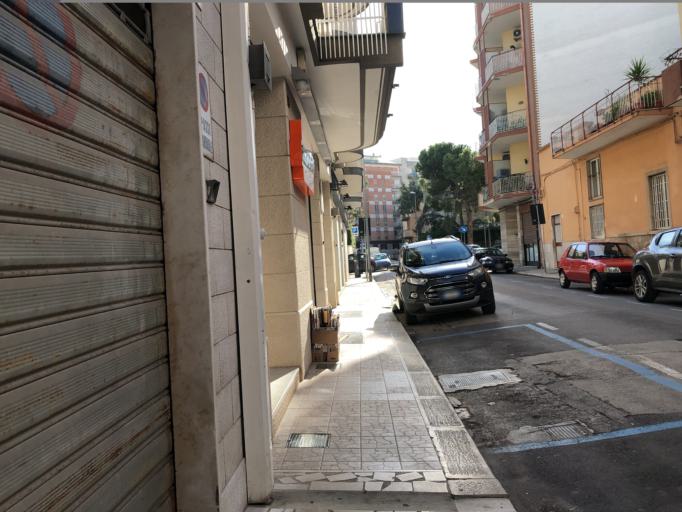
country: IT
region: Apulia
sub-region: Provincia di Barletta - Andria - Trani
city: Andria
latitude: 41.2298
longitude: 16.3048
